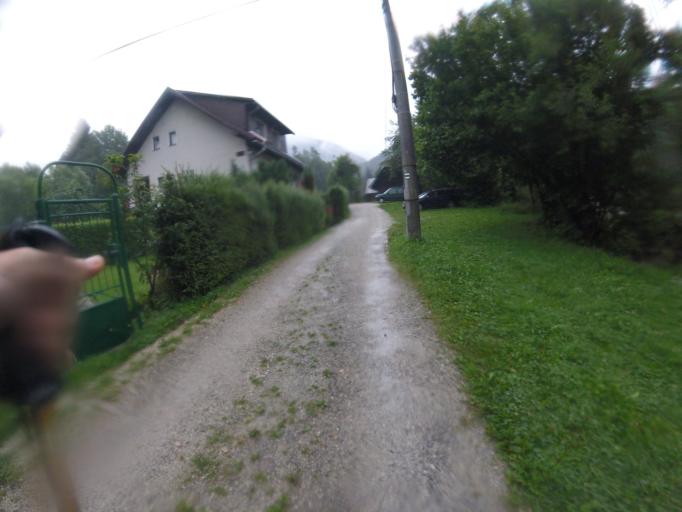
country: SK
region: Zilinsky
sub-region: Okres Zilina
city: Terchova
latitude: 49.2575
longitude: 19.0671
